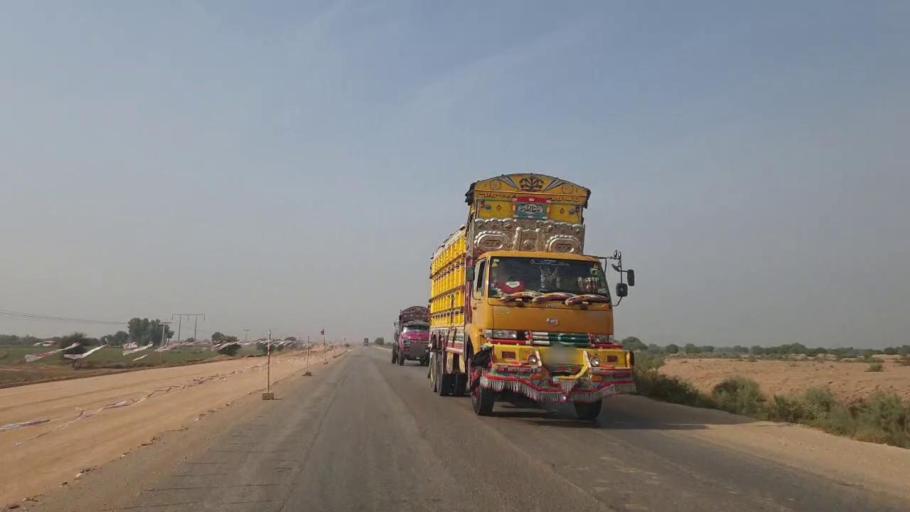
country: PK
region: Sindh
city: Sann
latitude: 26.1385
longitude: 68.0410
